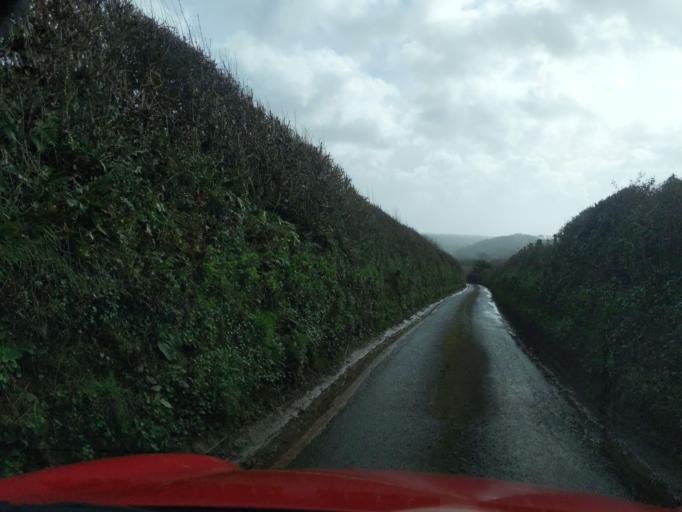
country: GB
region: England
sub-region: Devon
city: Ivybridge
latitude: 50.3610
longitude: -3.9290
